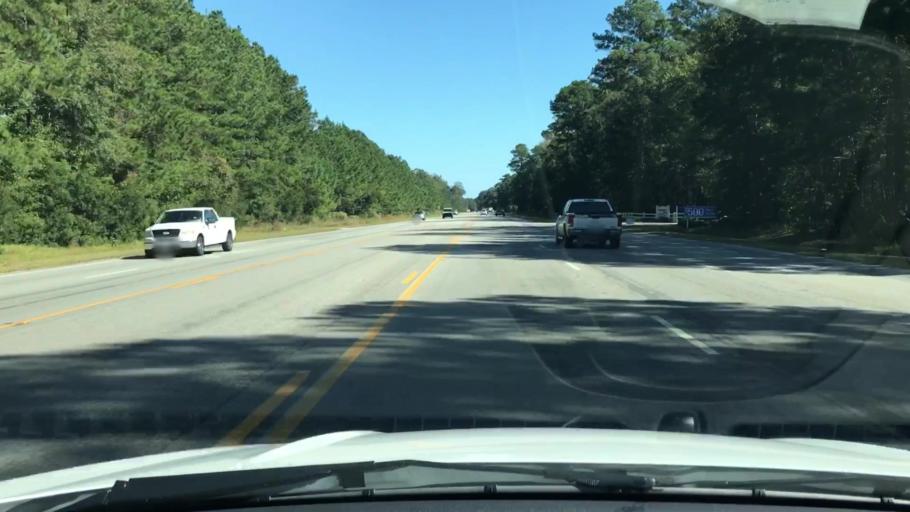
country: US
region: South Carolina
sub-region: Beaufort County
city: Bluffton
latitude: 32.3541
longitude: -80.9053
